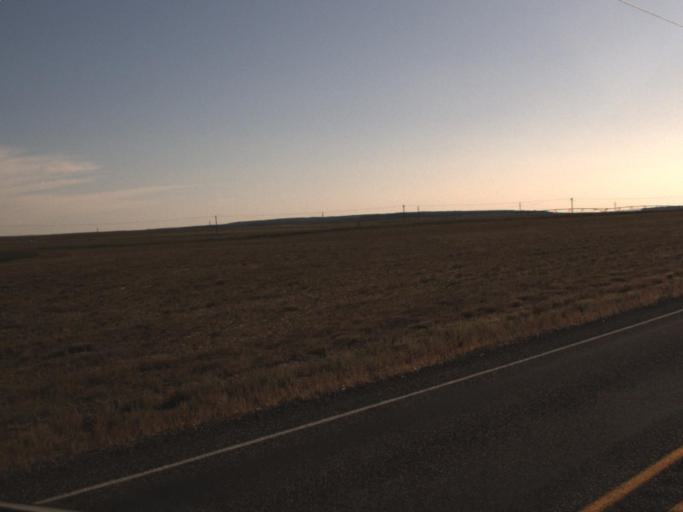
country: US
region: Washington
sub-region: Walla Walla County
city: Burbank
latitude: 46.2445
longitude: -118.8211
